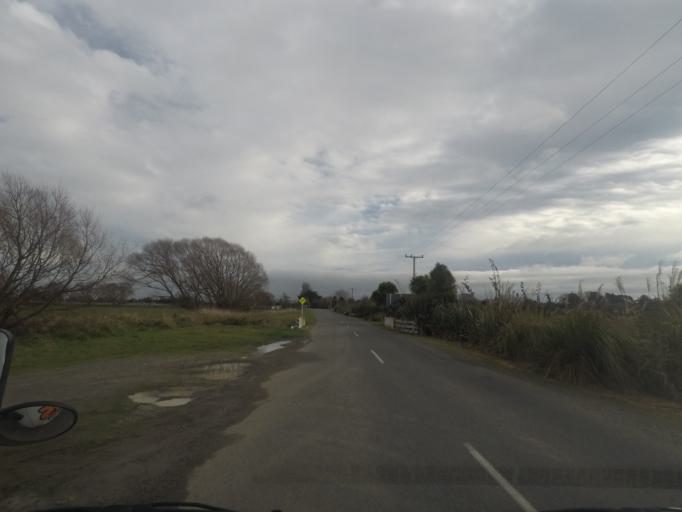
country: NZ
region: Canterbury
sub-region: Waimakariri District
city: Woodend
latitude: -43.2872
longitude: 172.7130
